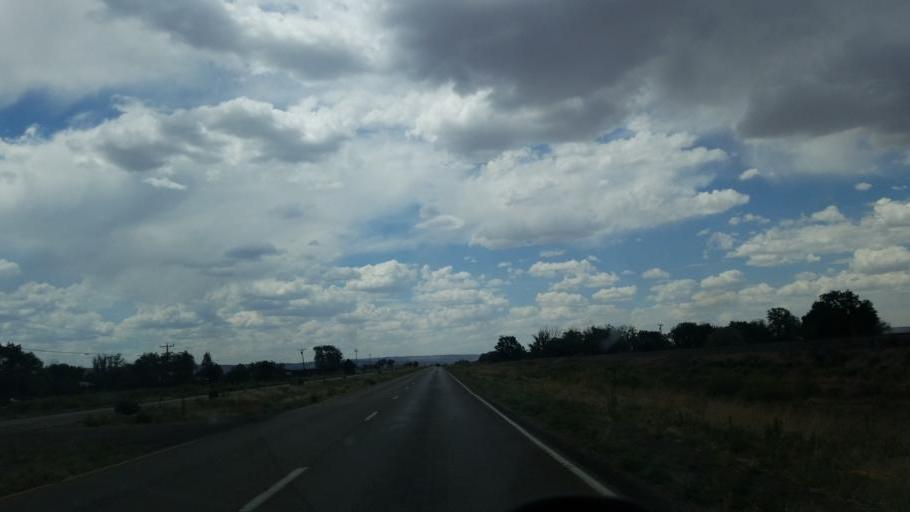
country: US
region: New Mexico
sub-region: Cibola County
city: Milan
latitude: 35.2307
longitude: -107.9293
